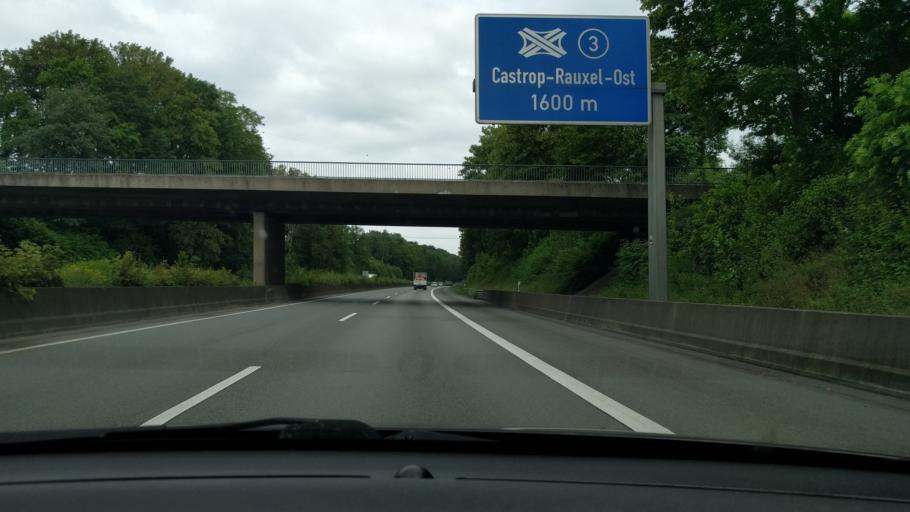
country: DE
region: North Rhine-Westphalia
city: Castrop-Rauxel
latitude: 51.5407
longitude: 7.3644
